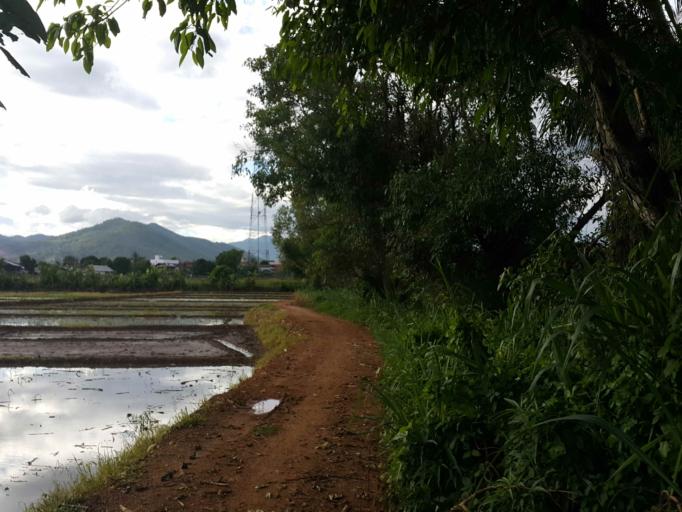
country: TH
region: Chiang Mai
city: Mae Chaem
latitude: 18.4933
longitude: 98.3665
